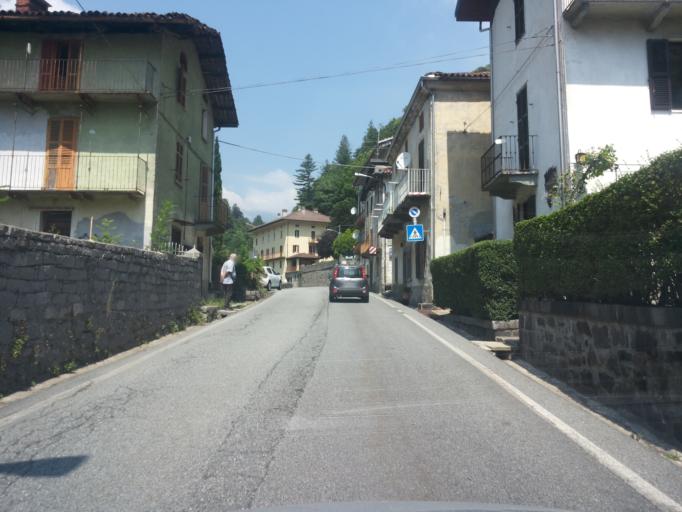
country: IT
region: Piedmont
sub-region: Provincia di Biella
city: San Paolo Cervo
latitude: 45.6472
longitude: 8.0177
